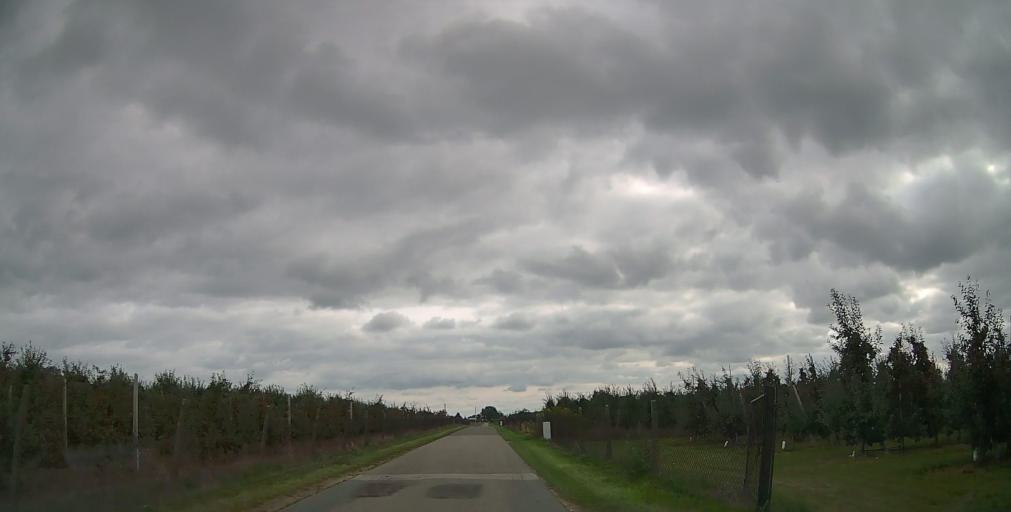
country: PL
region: Masovian Voivodeship
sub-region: Powiat grojecki
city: Goszczyn
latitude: 51.7662
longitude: 20.8682
